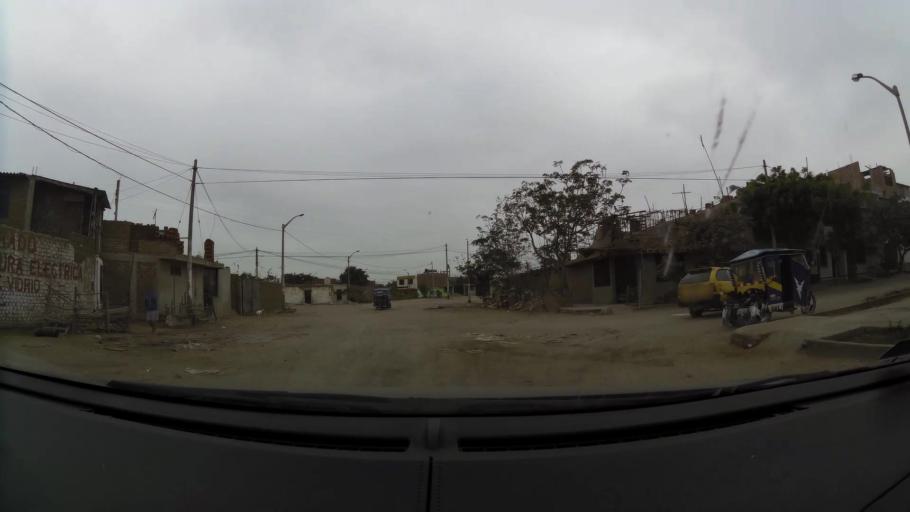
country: PE
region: La Libertad
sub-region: Provincia de Trujillo
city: La Esperanza
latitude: -8.0772
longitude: -79.0600
